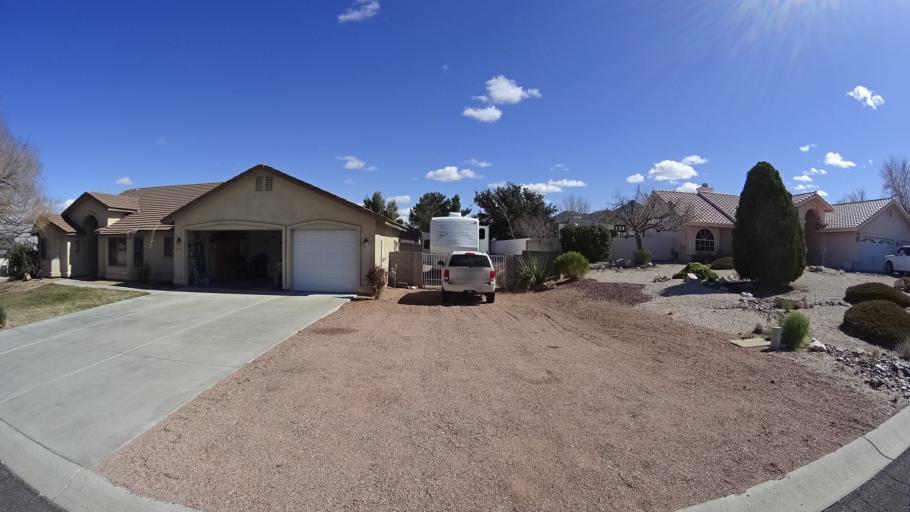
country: US
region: Arizona
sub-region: Mohave County
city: Kingman
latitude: 35.2000
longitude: -113.9721
